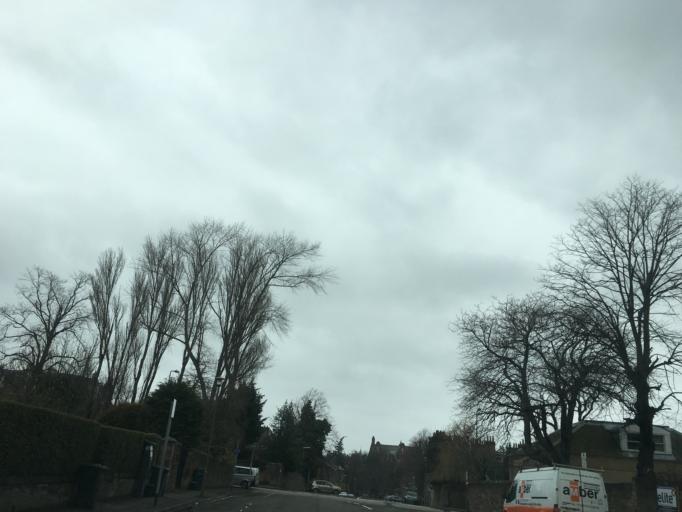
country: GB
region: Scotland
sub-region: Edinburgh
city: Edinburgh
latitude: 55.9352
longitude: -3.1873
